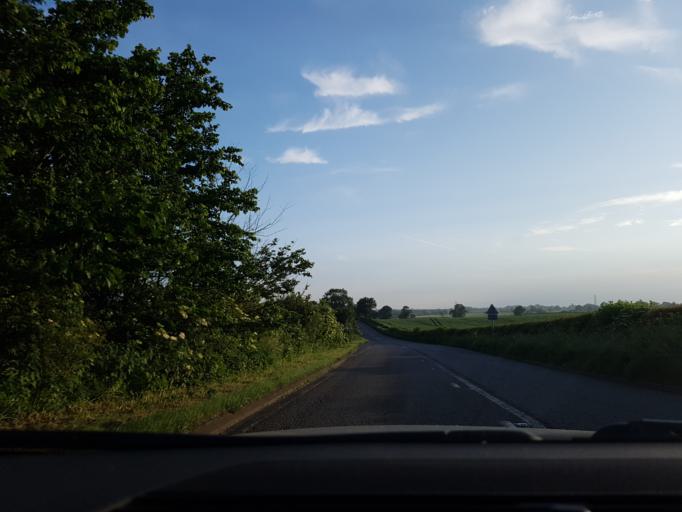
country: GB
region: England
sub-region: Northamptonshire
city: Deanshanger
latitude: 52.0192
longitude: -0.9316
